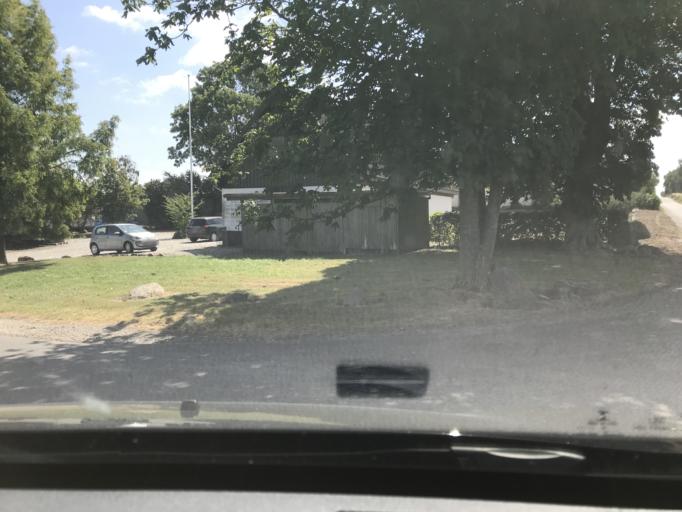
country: DK
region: South Denmark
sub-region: AEro Kommune
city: AEroskobing
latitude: 54.9081
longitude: 10.2999
